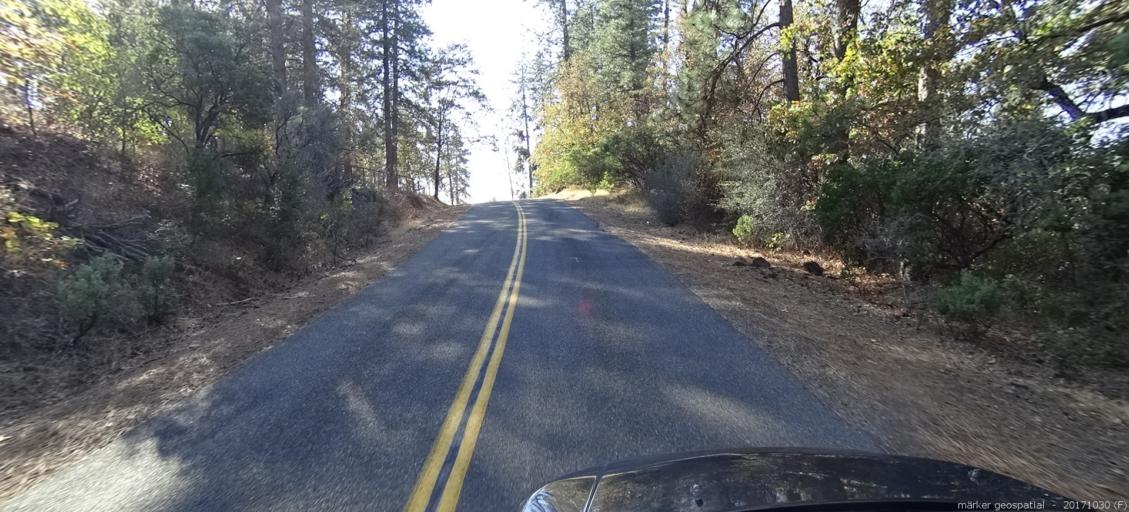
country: US
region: California
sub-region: Shasta County
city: Shingletown
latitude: 40.6524
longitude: -121.9441
